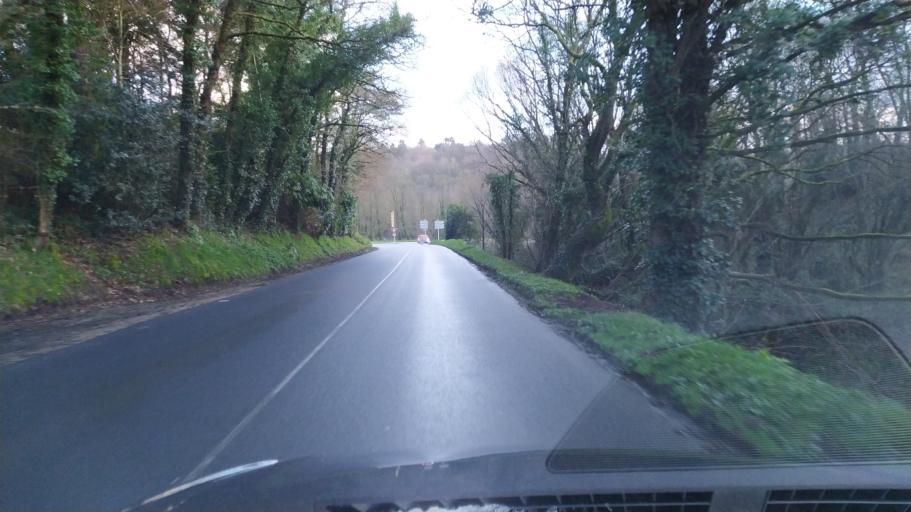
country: FR
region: Brittany
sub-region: Departement du Finistere
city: Landivisiau
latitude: 48.5000
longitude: -4.0942
